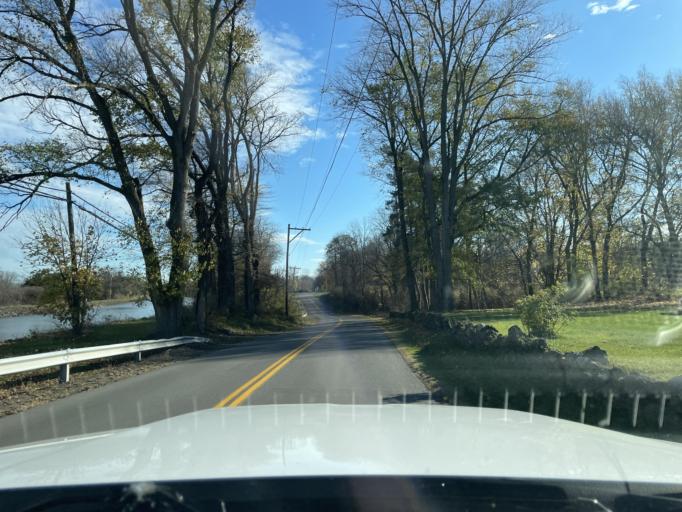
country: US
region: New York
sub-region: Niagara County
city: Gasport
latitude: 43.2010
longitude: -78.5616
